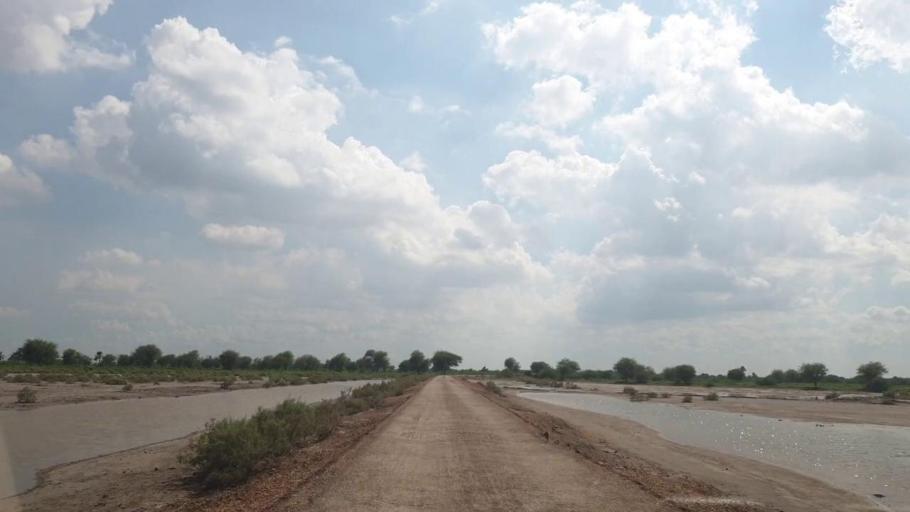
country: PK
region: Sindh
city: Pithoro
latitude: 25.5786
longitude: 69.3829
